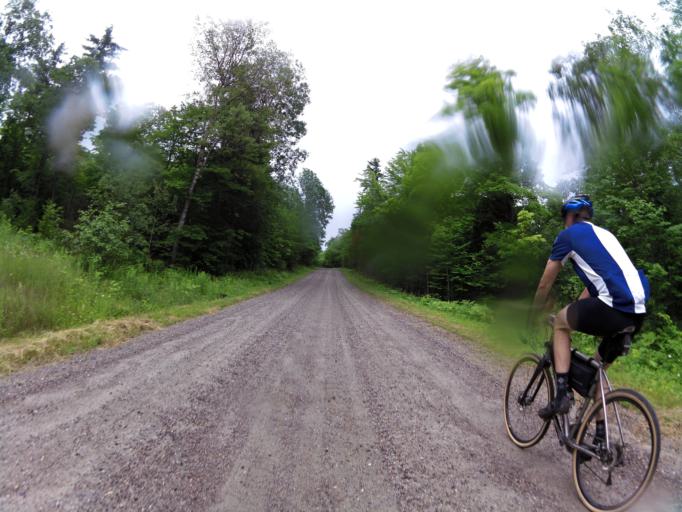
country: CA
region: Ontario
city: Renfrew
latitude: 45.0947
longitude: -76.5944
